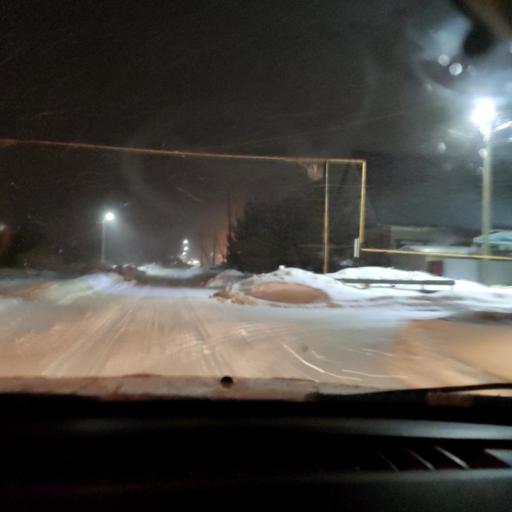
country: RU
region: Bashkortostan
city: Iglino
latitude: 54.8259
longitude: 56.3827
